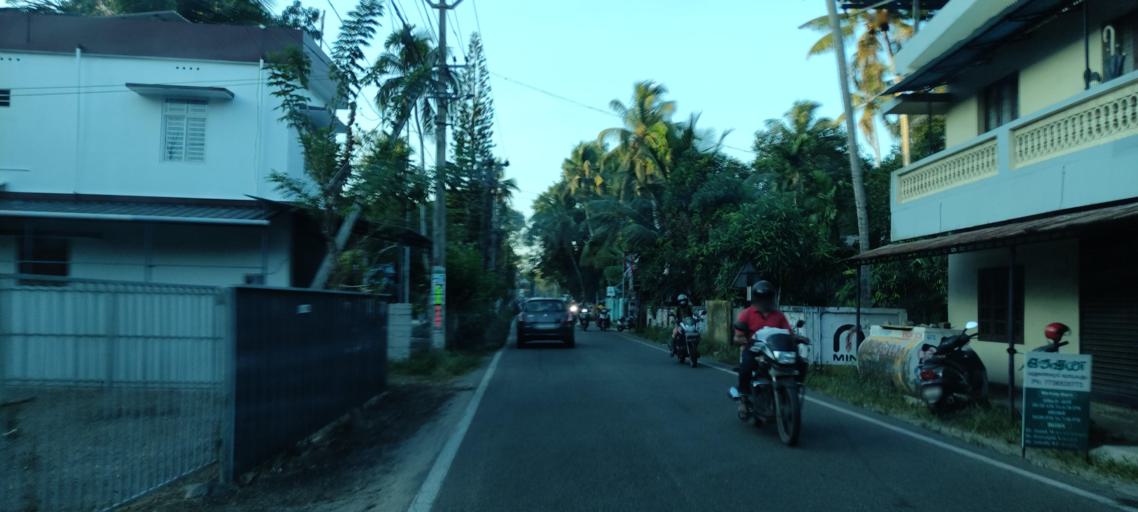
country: IN
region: Kerala
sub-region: Alappuzha
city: Kayankulam
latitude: 9.2342
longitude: 76.4563
